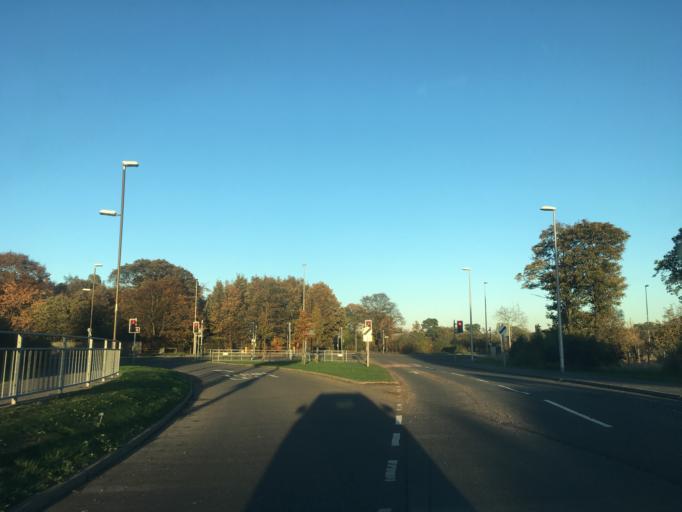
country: GB
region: Scotland
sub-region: Midlothian
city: Loanhead
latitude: 55.8688
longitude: -3.1912
